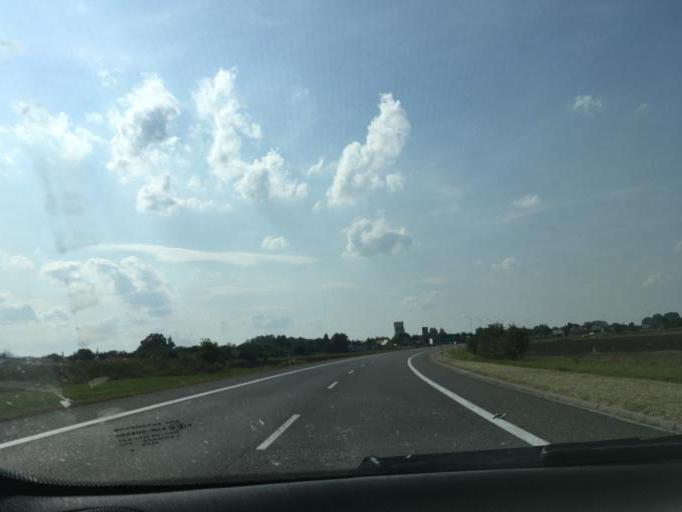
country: PL
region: Opole Voivodeship
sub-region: Powiat prudnicki
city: Lubrza
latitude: 50.3286
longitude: 17.6068
